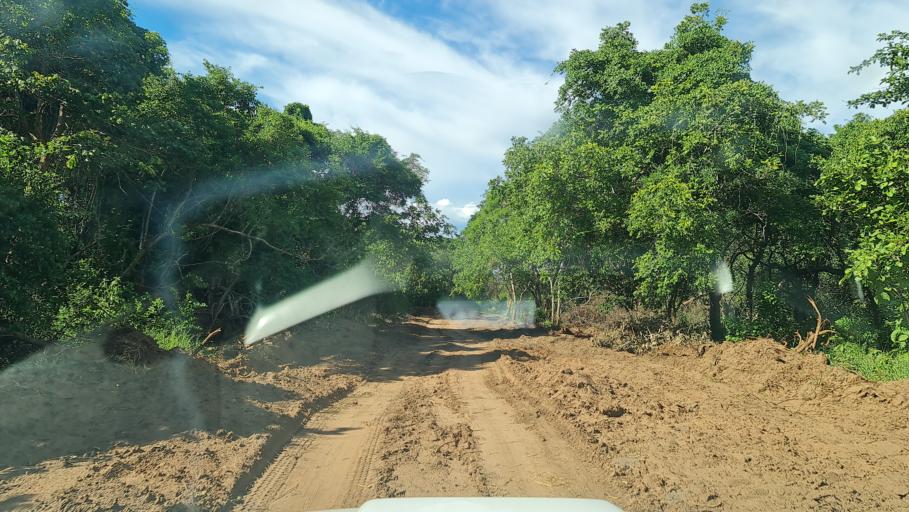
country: MZ
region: Nampula
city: Antonio Enes
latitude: -15.5129
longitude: 40.1314
